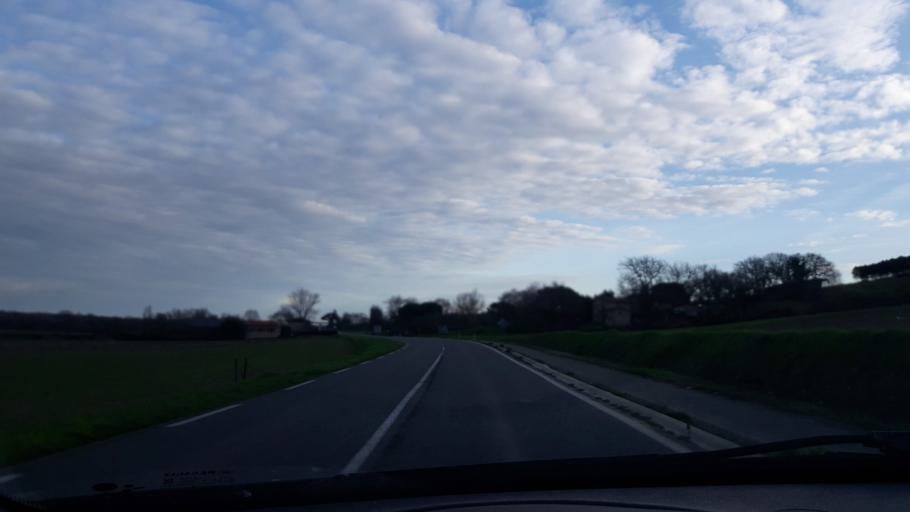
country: FR
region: Midi-Pyrenees
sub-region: Departement de la Haute-Garonne
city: Levignac
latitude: 43.6725
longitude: 1.2026
